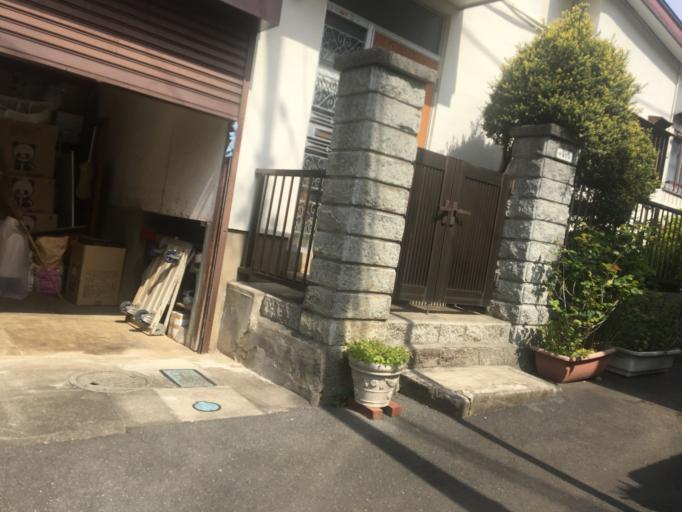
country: JP
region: Saitama
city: Shiki
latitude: 35.8197
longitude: 139.5603
